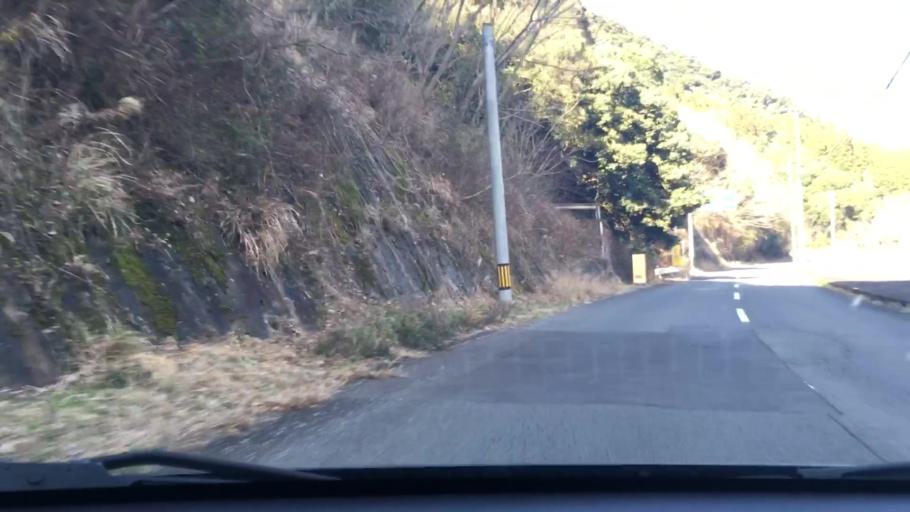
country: JP
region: Kagoshima
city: Ijuin
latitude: 31.7447
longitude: 130.4090
